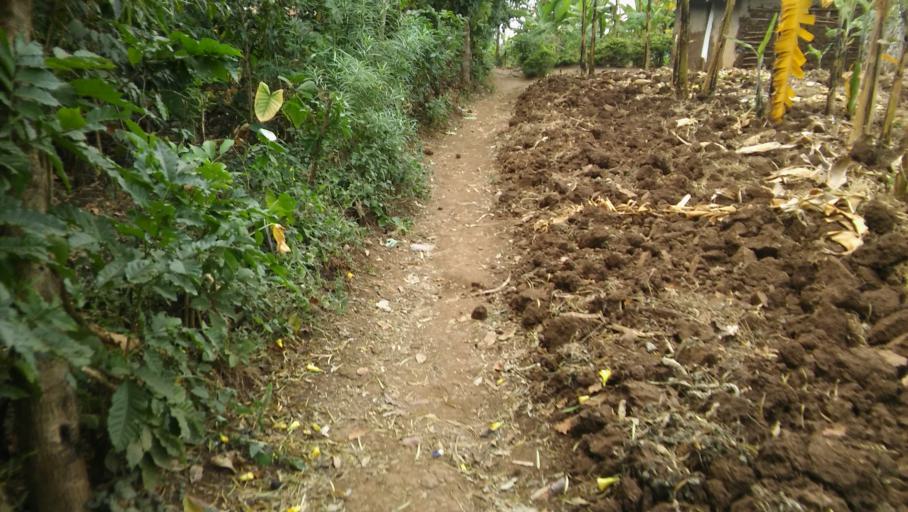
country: UG
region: Eastern Region
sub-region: Mbale District
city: Mbale
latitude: 1.0578
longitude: 34.2147
